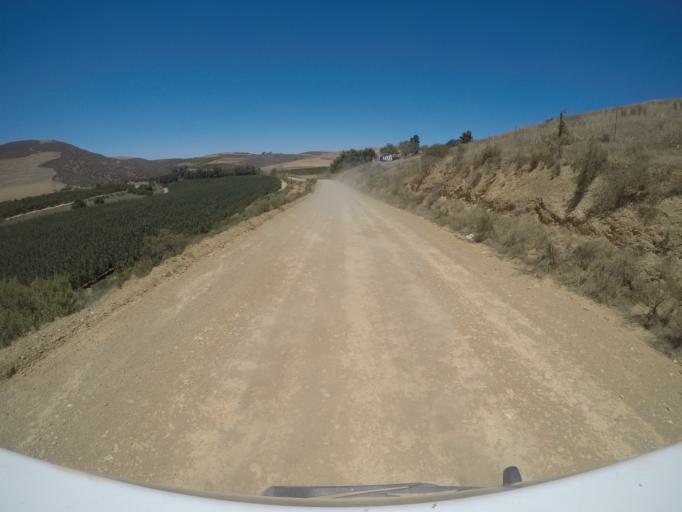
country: ZA
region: Western Cape
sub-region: Overberg District Municipality
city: Grabouw
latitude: -34.1068
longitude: 19.2105
